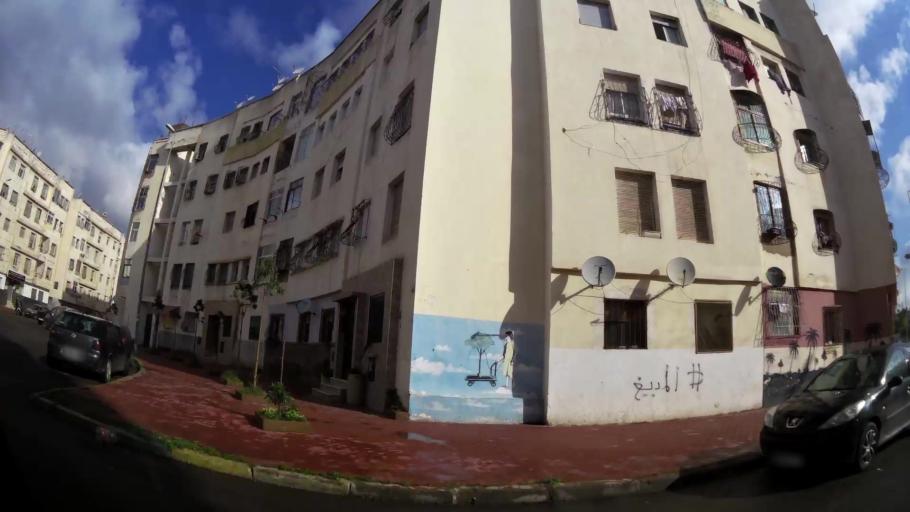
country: MA
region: Grand Casablanca
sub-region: Mediouna
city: Tit Mellil
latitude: 33.5949
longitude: -7.5359
